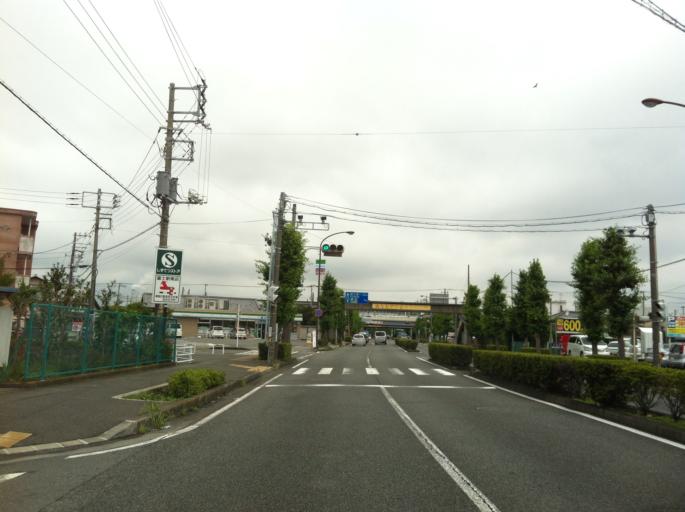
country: JP
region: Shizuoka
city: Fuji
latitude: 35.1398
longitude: 138.6625
